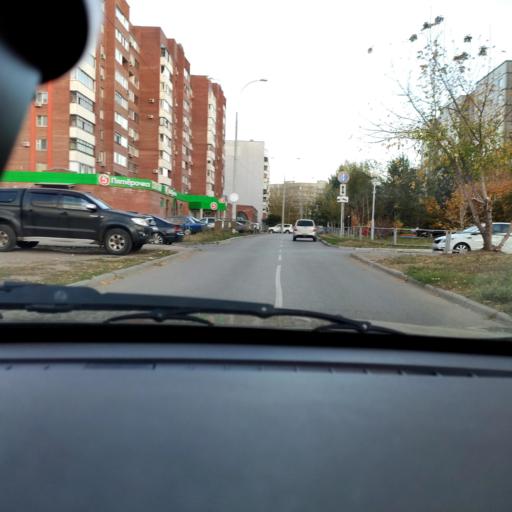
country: RU
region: Samara
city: Tol'yatti
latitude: 53.5462
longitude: 49.3320
